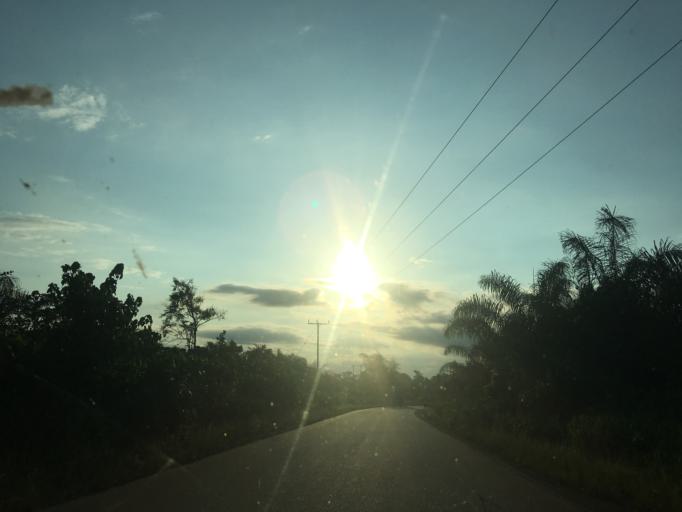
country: GH
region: Western
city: Bibiani
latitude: 6.6009
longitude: -2.3977
